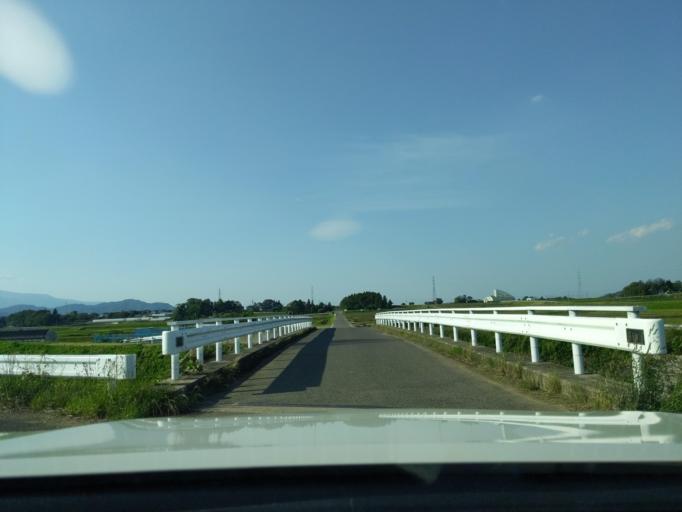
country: JP
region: Fukushima
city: Koriyama
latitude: 37.4474
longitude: 140.3650
